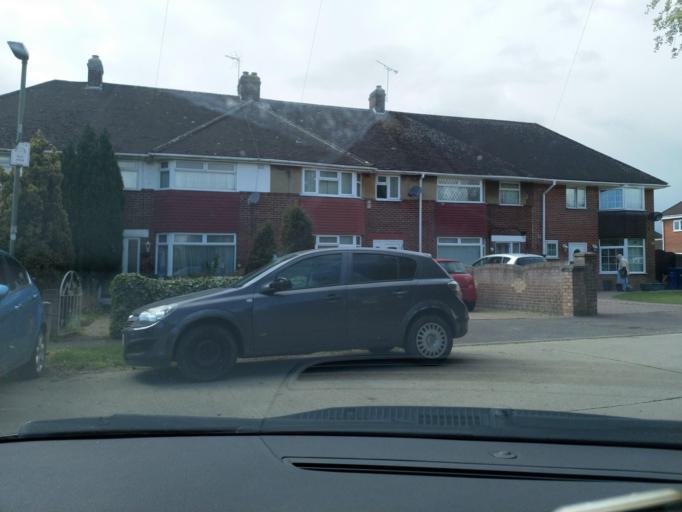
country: GB
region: England
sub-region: Suffolk
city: Woodbridge
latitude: 52.0695
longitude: 1.3233
